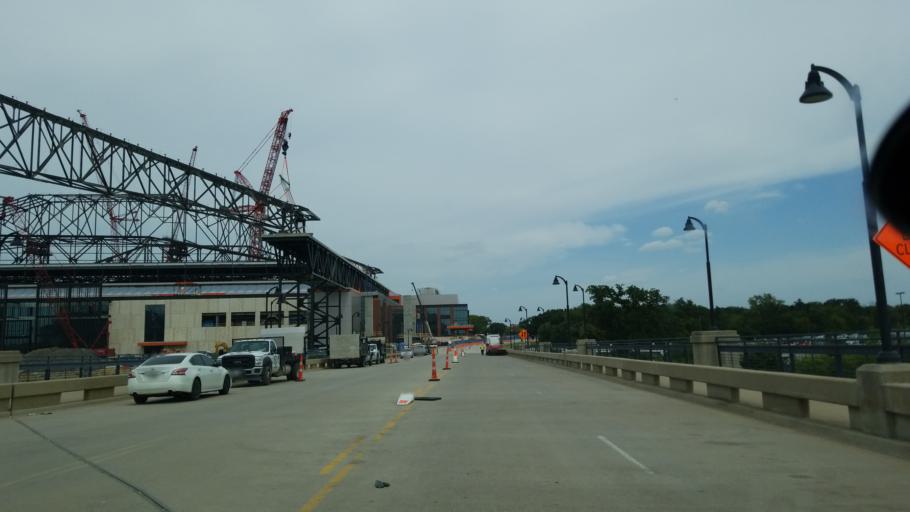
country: US
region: Texas
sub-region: Tarrant County
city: Arlington
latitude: 32.7462
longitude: -97.0877
